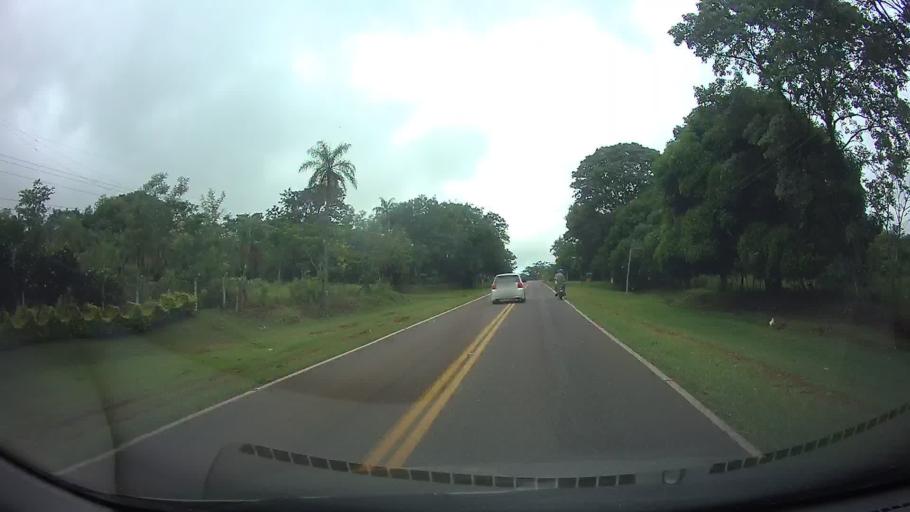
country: PY
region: Paraguari
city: Acahay
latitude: -25.9317
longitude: -57.1056
